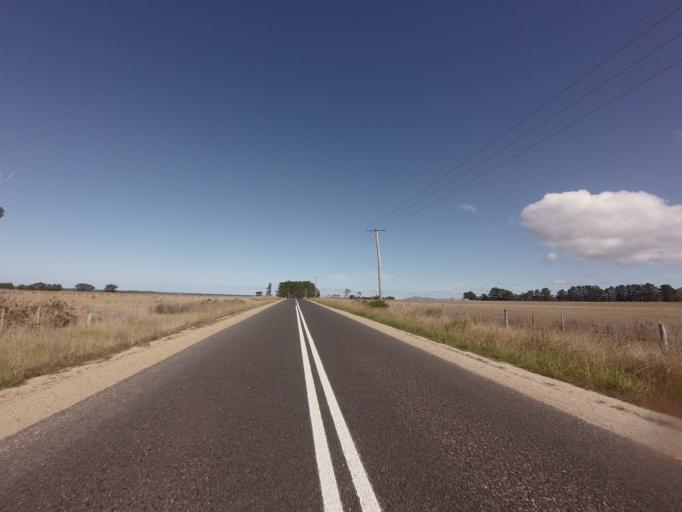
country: AU
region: Tasmania
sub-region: Break O'Day
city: St Helens
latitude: -41.7460
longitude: 148.2752
